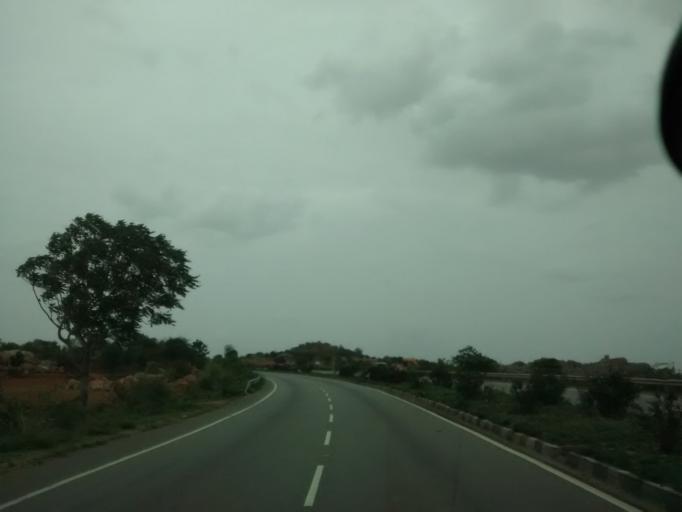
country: IN
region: Andhra Pradesh
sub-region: Kurnool
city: Ramapuram
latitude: 15.1995
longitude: 77.7109
